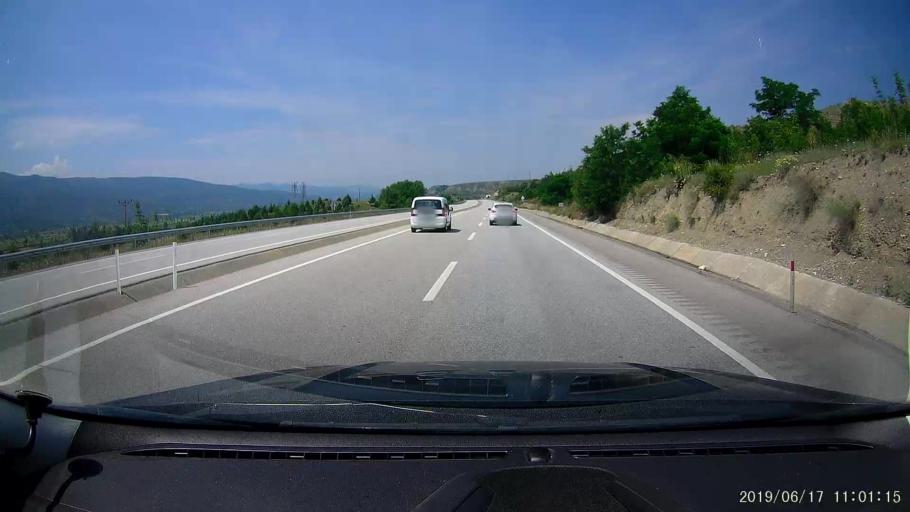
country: TR
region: Kastamonu
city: Tosya
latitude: 41.0285
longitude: 34.1605
